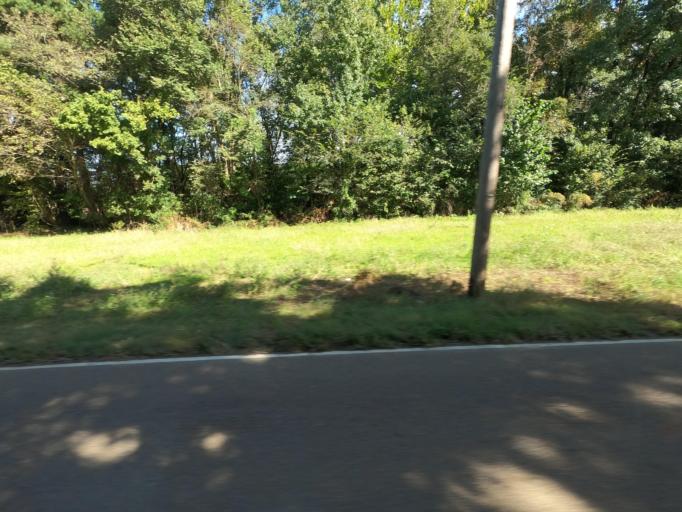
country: US
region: Tennessee
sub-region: Fayette County
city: Hickory Withe
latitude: 35.2311
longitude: -89.6499
